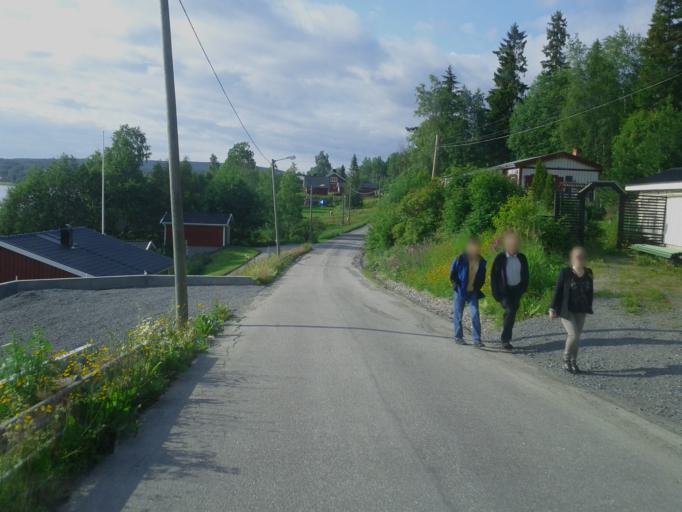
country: SE
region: Vaesternorrland
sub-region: OErnskoeldsviks Kommun
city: Ornskoldsvik
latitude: 63.2580
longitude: 18.8093
